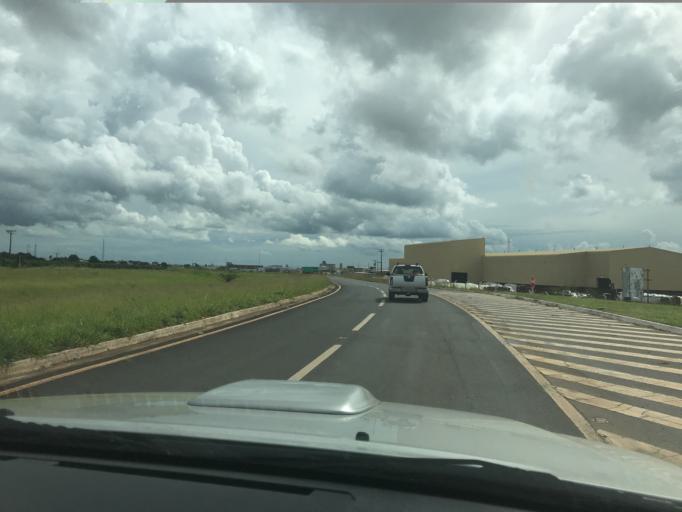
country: BR
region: Minas Gerais
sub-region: Patrocinio
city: Patrocinio
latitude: -19.0964
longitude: -46.6723
